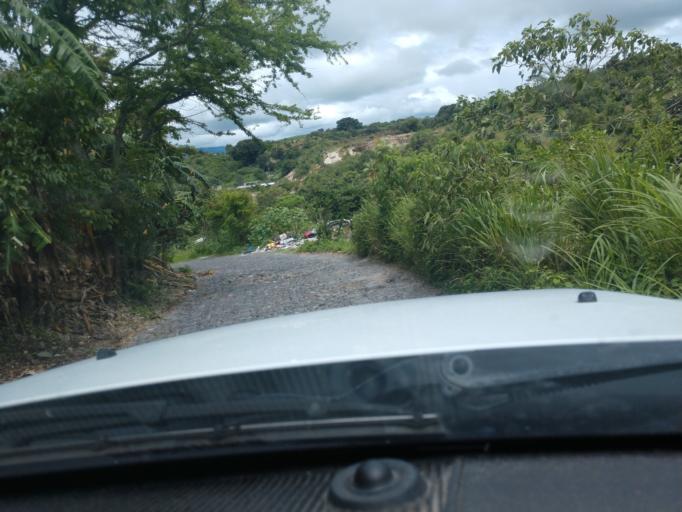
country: MX
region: Nayarit
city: Xalisco
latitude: 21.4414
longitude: -104.9104
